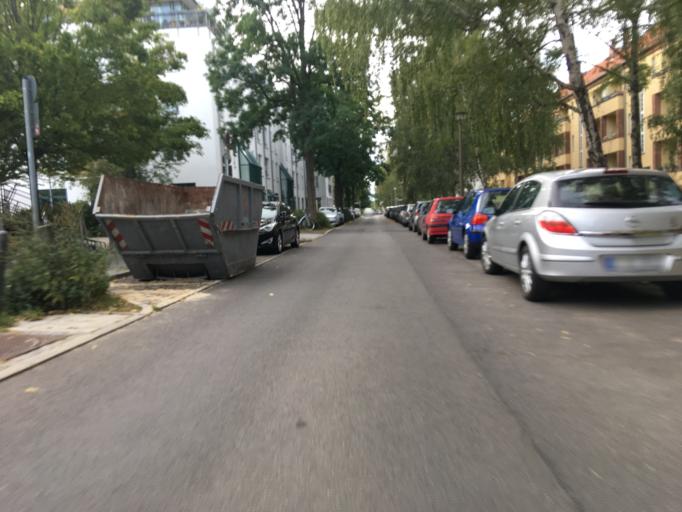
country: DE
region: Berlin
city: Heinersdorf
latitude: 52.5585
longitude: 13.4435
